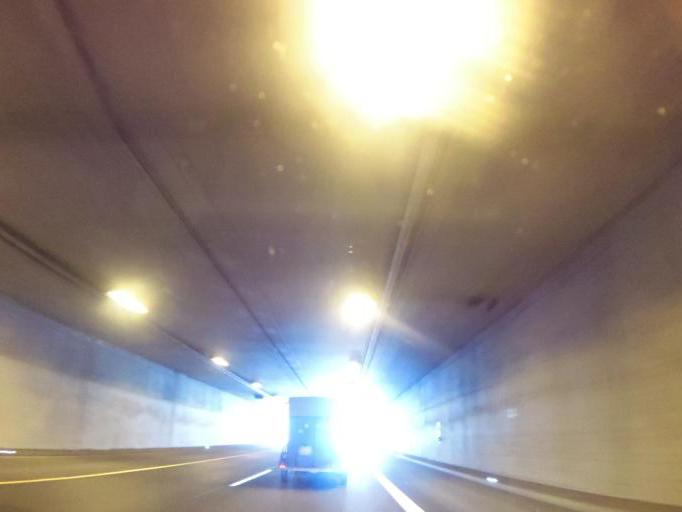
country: DE
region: Baden-Wuerttemberg
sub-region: Regierungsbezirk Stuttgart
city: Gruibingen
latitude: 48.5965
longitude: 9.6455
